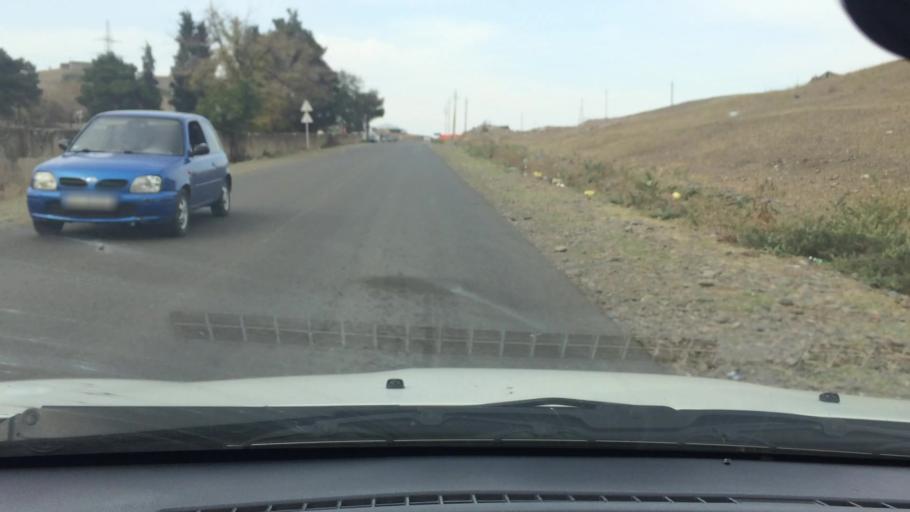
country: GE
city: Naghvarevi
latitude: 41.3613
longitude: 44.8372
